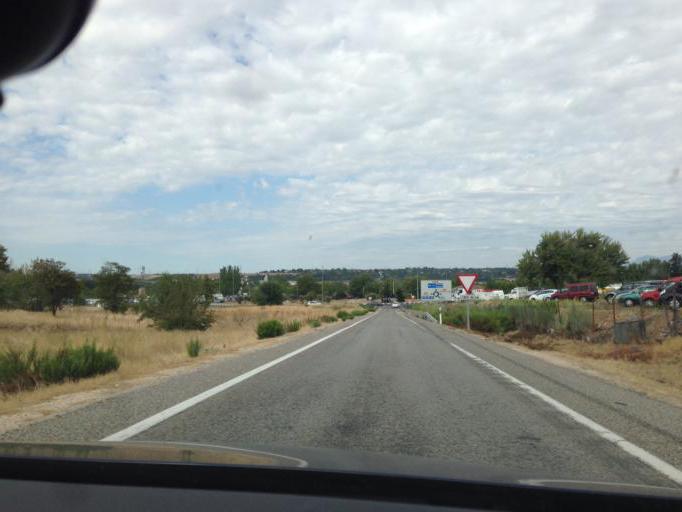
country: ES
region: Madrid
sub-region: Provincia de Madrid
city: Cobena
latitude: 40.5847
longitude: -3.5565
